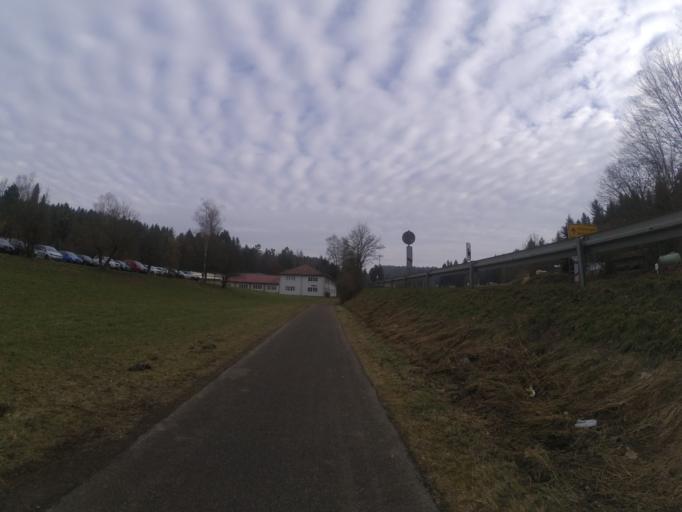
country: DE
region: Baden-Wuerttemberg
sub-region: Tuebingen Region
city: Mehrstetten
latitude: 48.3681
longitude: 9.5337
